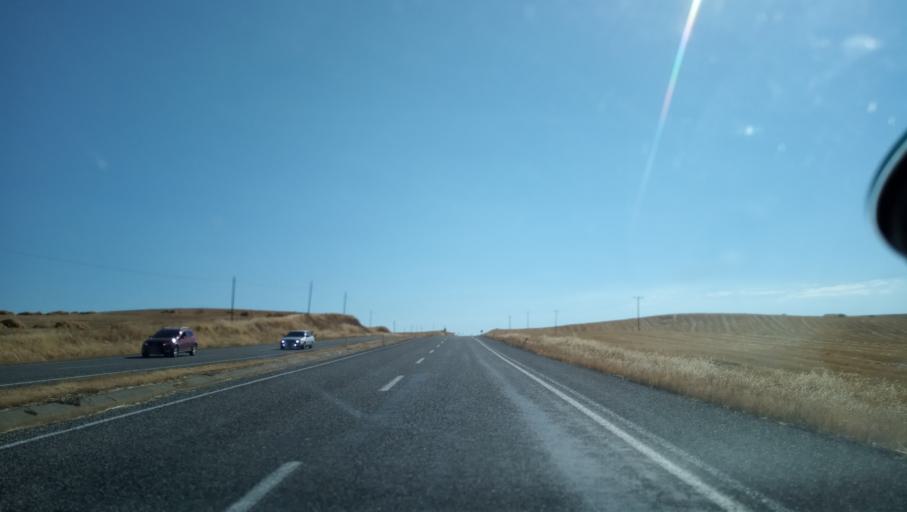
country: TR
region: Diyarbakir
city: Bagdere
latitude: 38.1285
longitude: 40.7553
